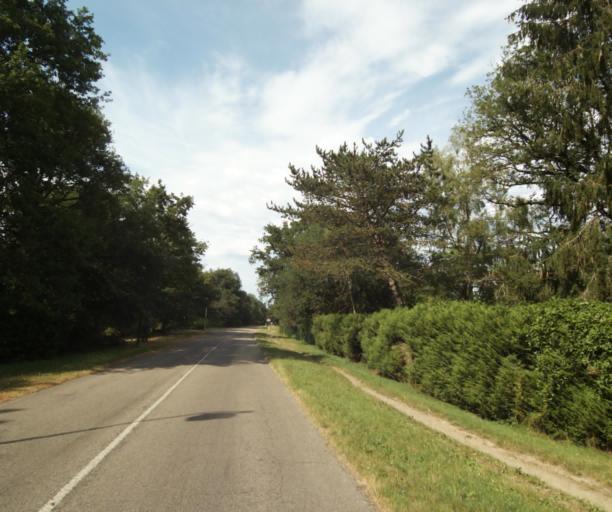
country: FR
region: Ile-de-France
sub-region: Departement de Seine-et-Marne
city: Acheres-la-Foret
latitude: 48.3594
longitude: 2.5632
